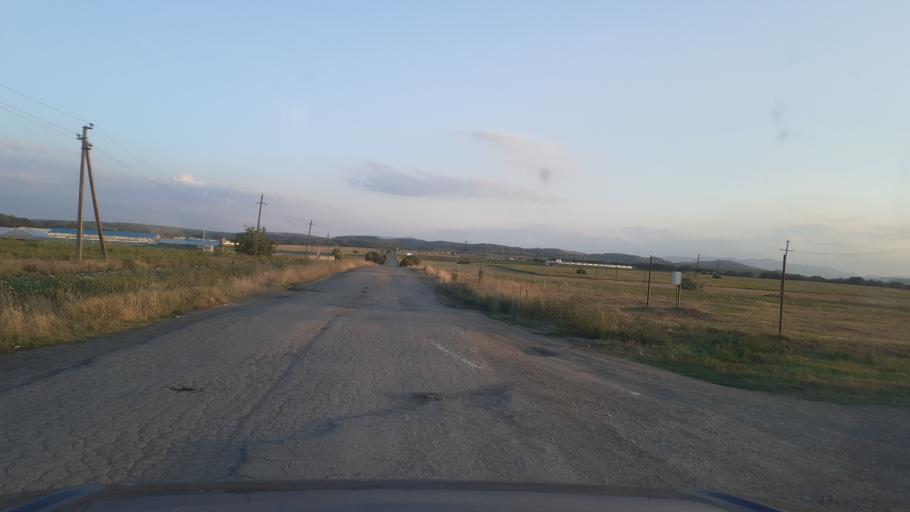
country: RU
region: Krasnodarskiy
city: Il'skiy
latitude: 44.8506
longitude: 38.6033
